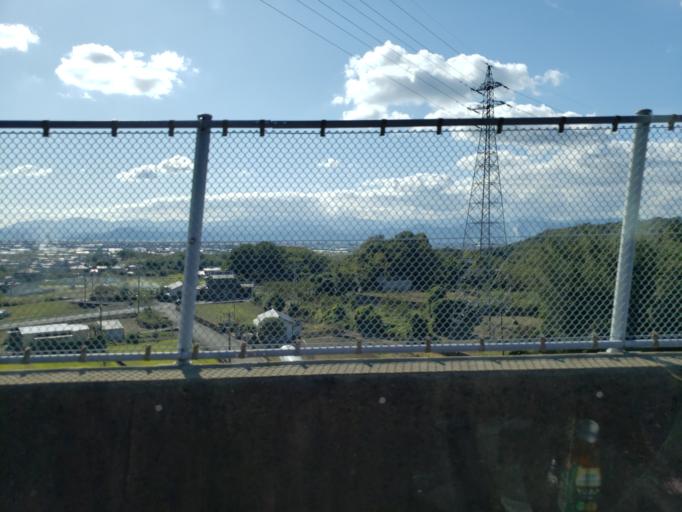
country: JP
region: Tokushima
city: Ishii
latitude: 34.1431
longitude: 134.4338
